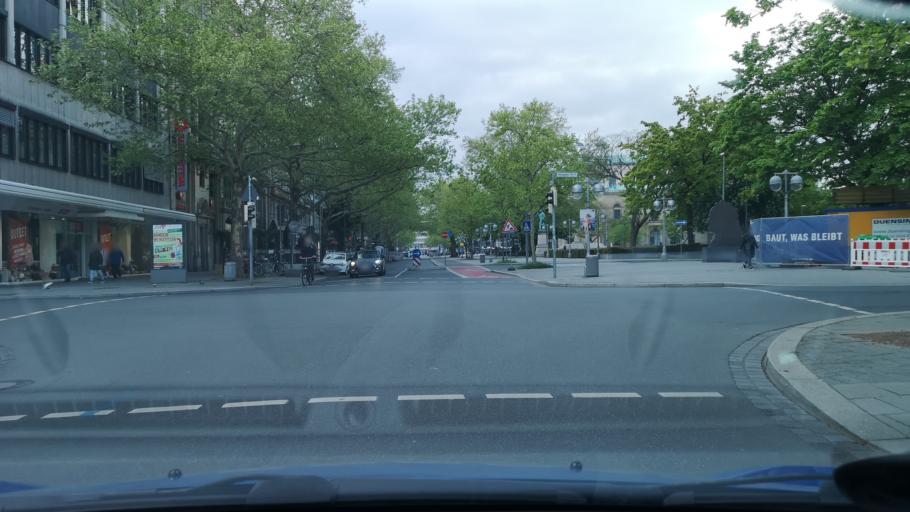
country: DE
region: Lower Saxony
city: Hannover
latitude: 52.3710
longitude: 9.7416
